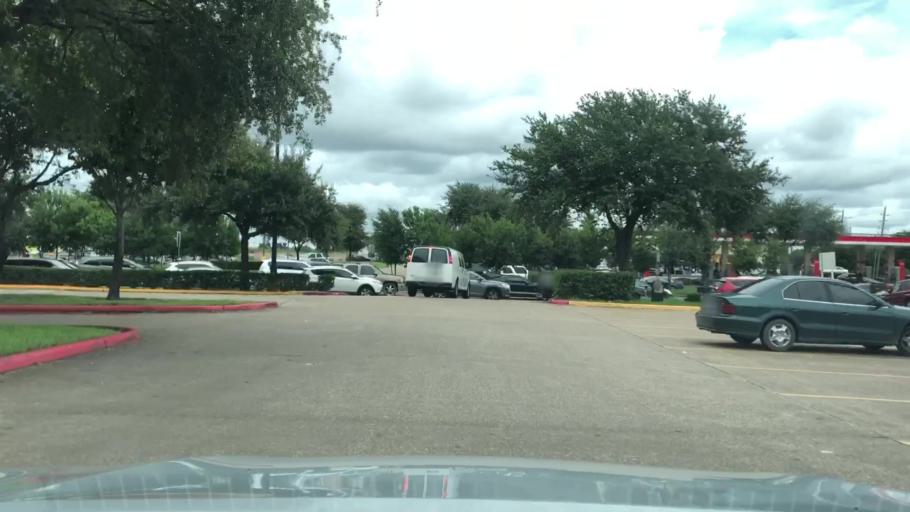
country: US
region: Texas
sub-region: Fort Bend County
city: Meadows Place
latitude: 29.6890
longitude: -95.5589
